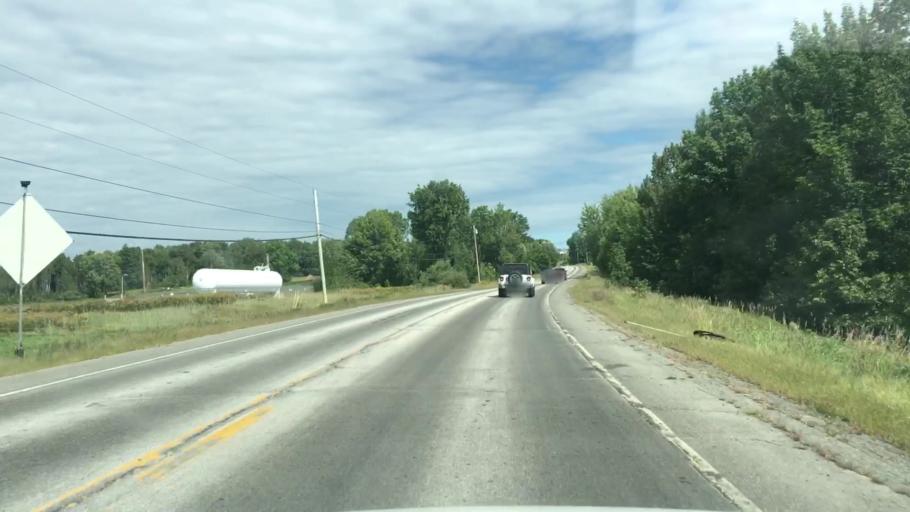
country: US
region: Maine
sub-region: Piscataquis County
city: Dover-Foxcroft
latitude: 45.1546
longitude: -69.2355
